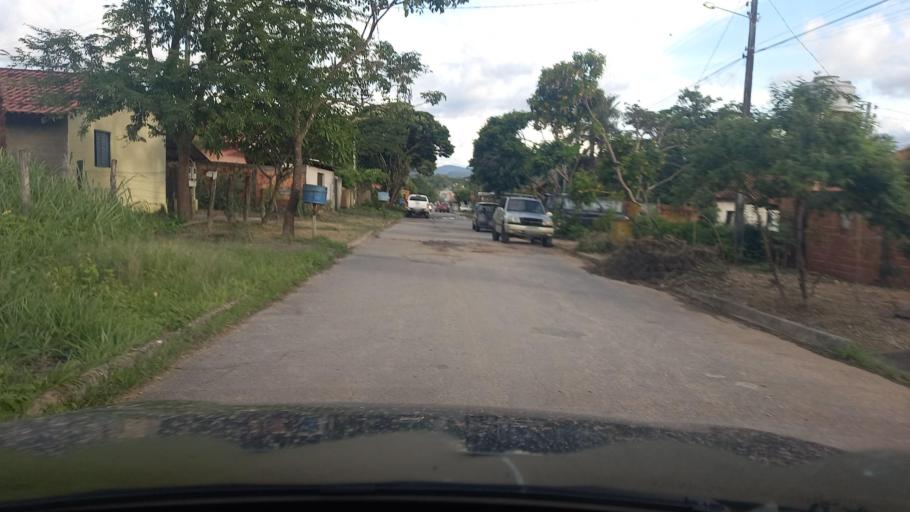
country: BR
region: Goias
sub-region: Cavalcante
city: Cavalcante
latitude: -13.7934
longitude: -47.4605
